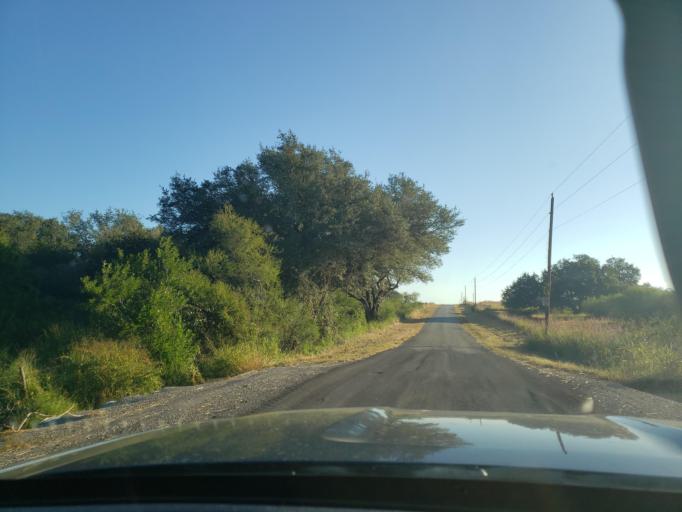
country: US
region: Texas
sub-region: Bee County
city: Beeville
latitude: 28.4248
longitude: -97.7028
